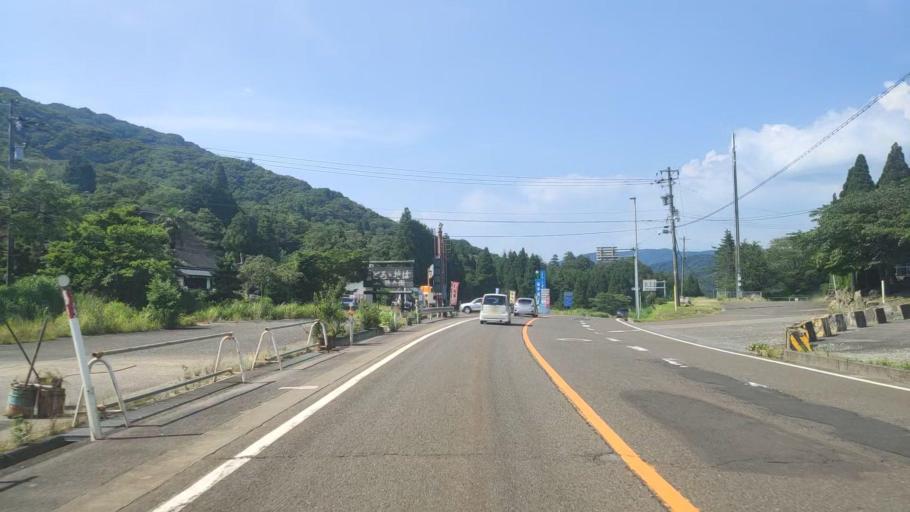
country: JP
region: Fukui
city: Tsuruga
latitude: 35.5771
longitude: 136.1226
